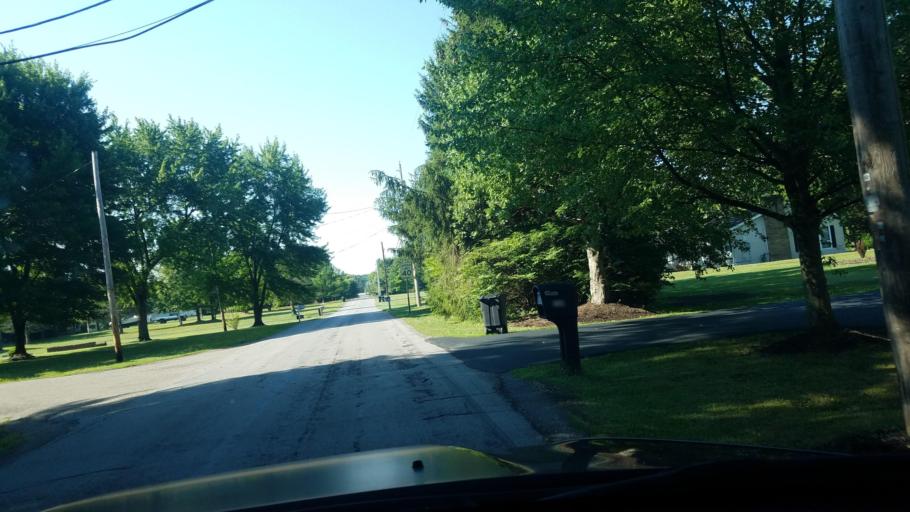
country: US
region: Ohio
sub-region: Trumbull County
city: Champion Heights
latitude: 41.3008
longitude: -80.8205
